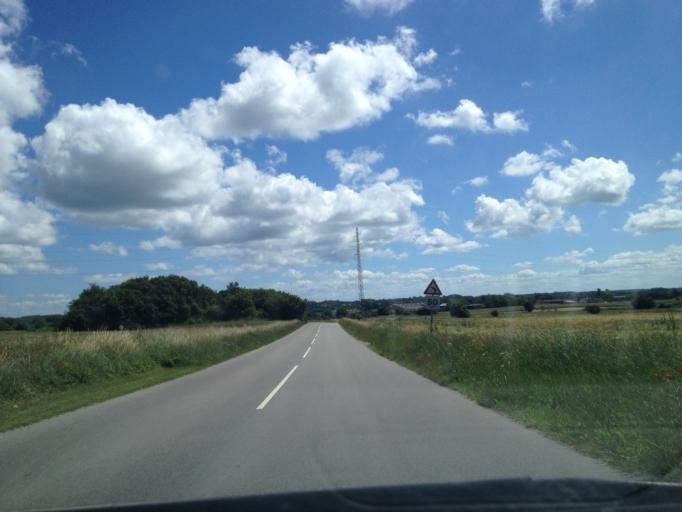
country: DK
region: Zealand
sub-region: Odsherred Kommune
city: Hojby
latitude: 55.9120
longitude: 11.5772
